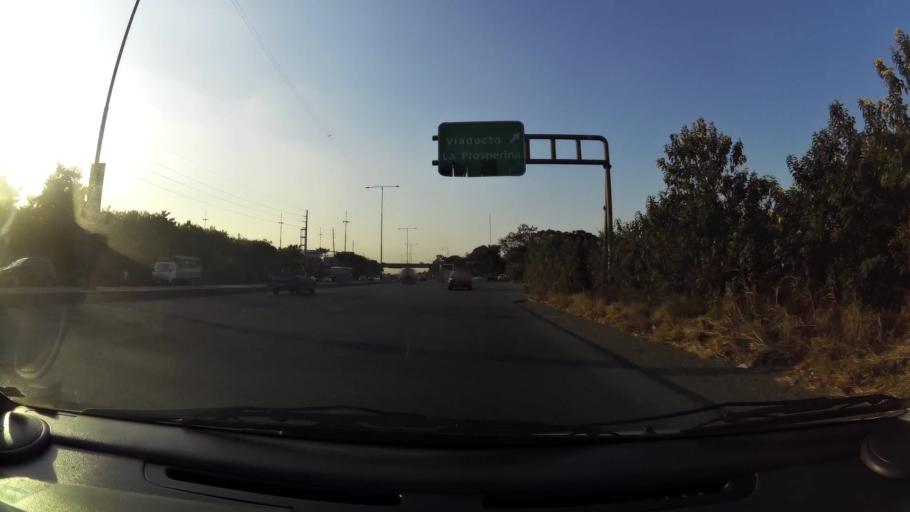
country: EC
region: Guayas
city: Santa Lucia
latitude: -2.1431
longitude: -79.9456
